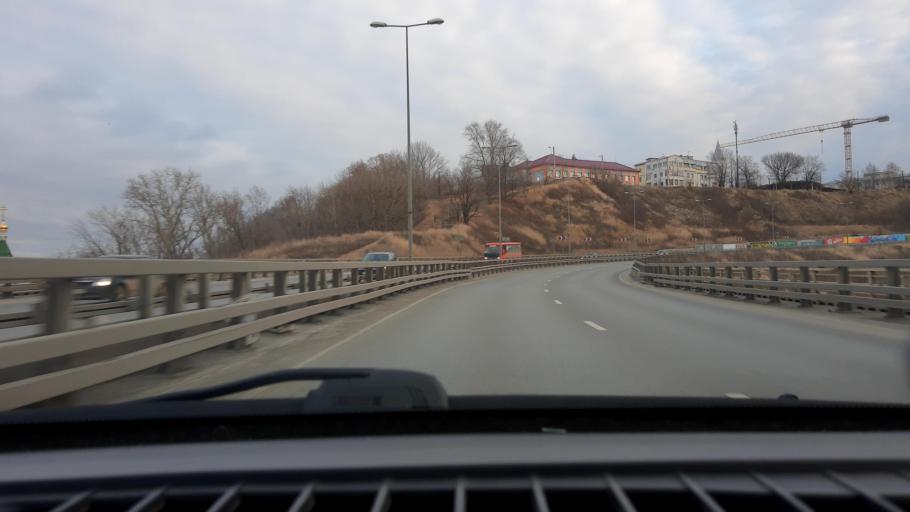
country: RU
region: Nizjnij Novgorod
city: Nizhniy Novgorod
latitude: 56.3154
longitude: 43.9730
